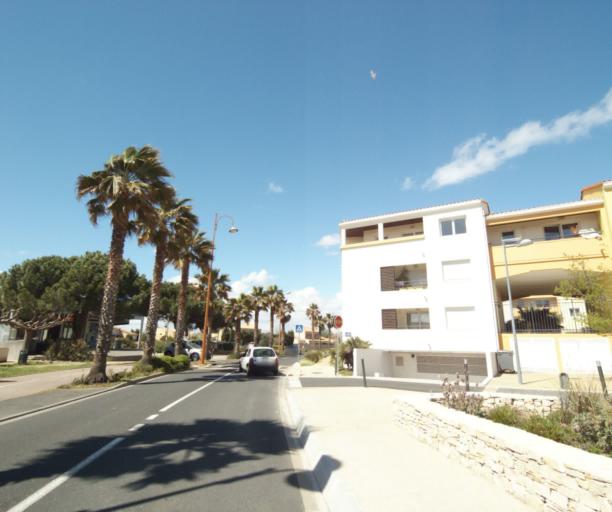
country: FR
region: Languedoc-Roussillon
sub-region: Departement de l'Herault
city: Perols
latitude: 43.5614
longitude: 3.9516
